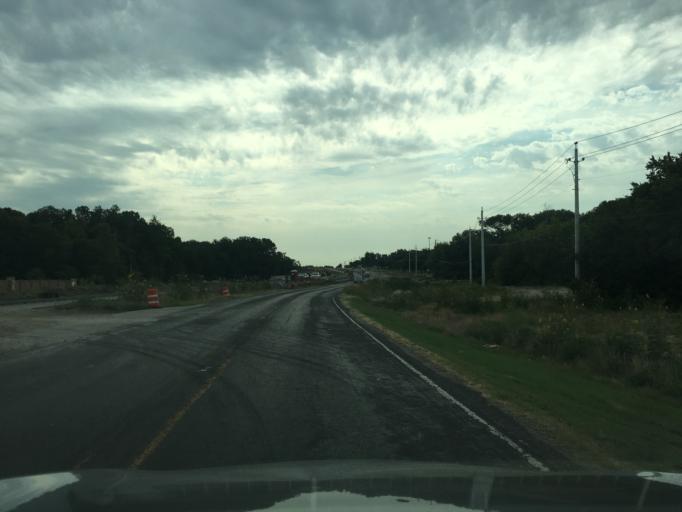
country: US
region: Texas
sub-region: Collin County
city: Lucas
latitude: 33.0550
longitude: -96.5778
